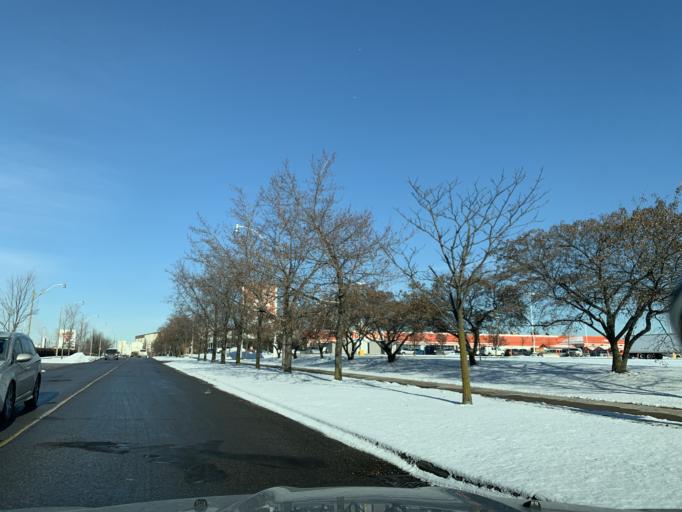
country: CA
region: Ontario
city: Toronto
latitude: 43.6693
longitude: -79.4699
